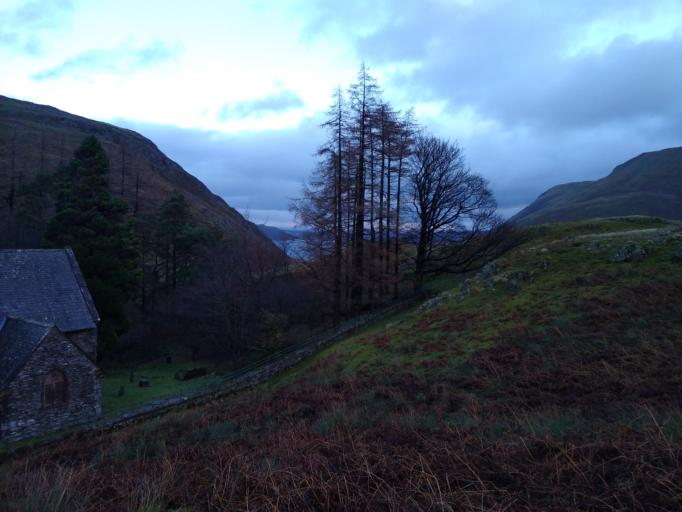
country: GB
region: England
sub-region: Cumbria
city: Penrith
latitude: 54.5641
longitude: -2.8735
